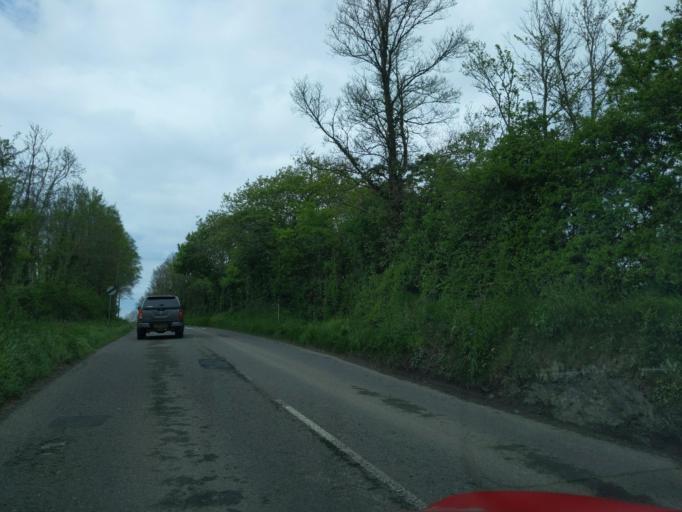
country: GB
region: England
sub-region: Cornwall
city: Wadebridge
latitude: 50.5284
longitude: -4.8340
